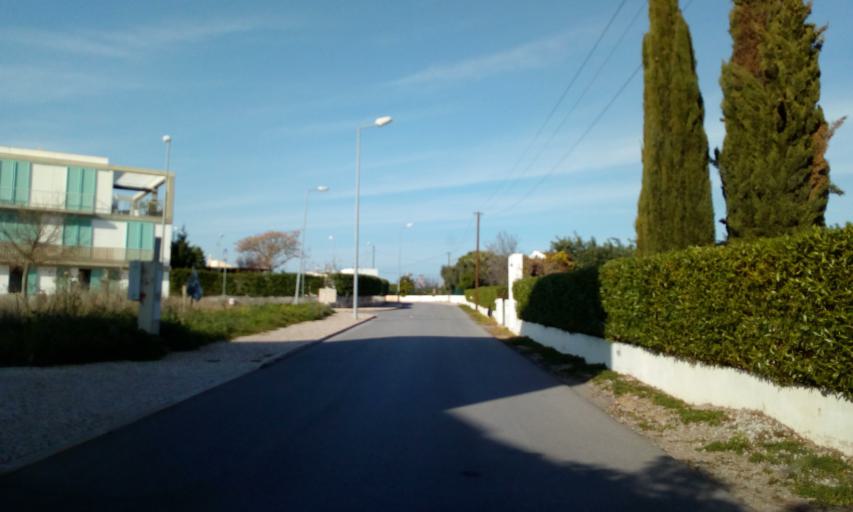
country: PT
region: Faro
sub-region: Tavira
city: Tavira
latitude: 37.1414
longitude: -7.5976
